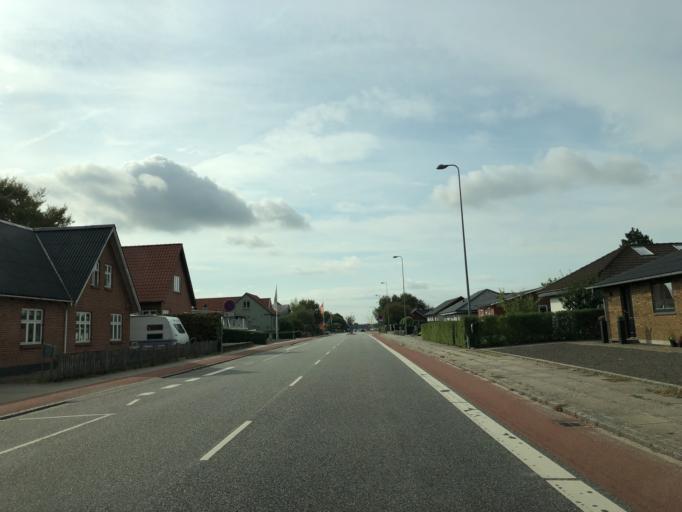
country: DK
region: Central Jutland
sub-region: Ringkobing-Skjern Kommune
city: Skjern
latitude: 55.9375
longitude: 8.5042
